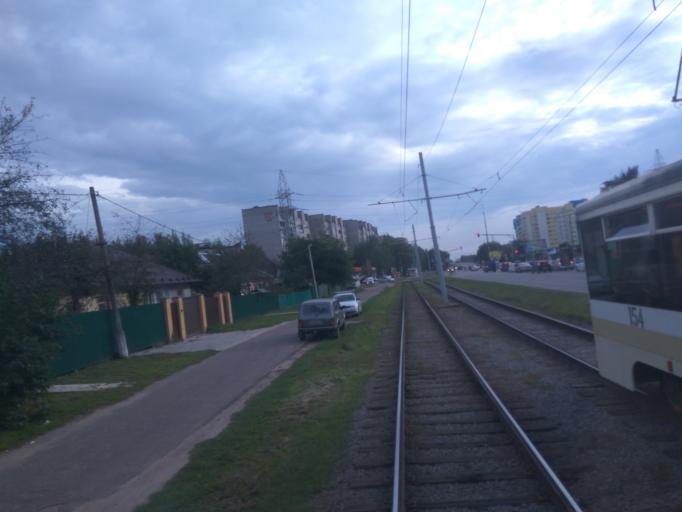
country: RU
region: Moskovskaya
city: Kolomna
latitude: 55.0785
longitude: 38.7621
